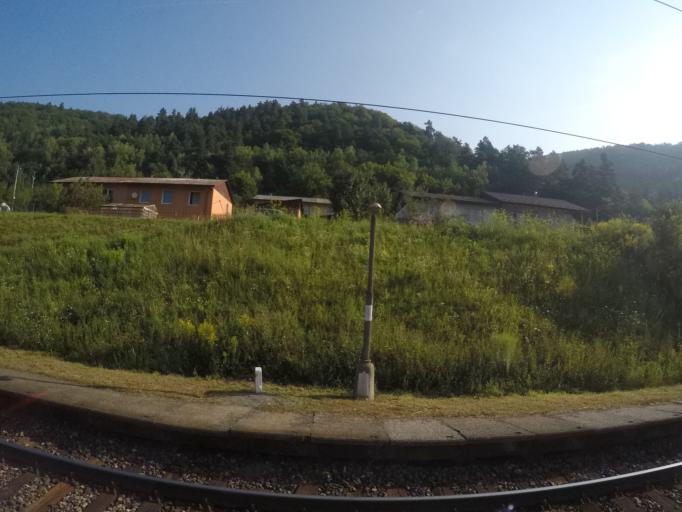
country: SK
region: Kosicky
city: Gelnica
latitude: 48.8894
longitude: 21.0414
